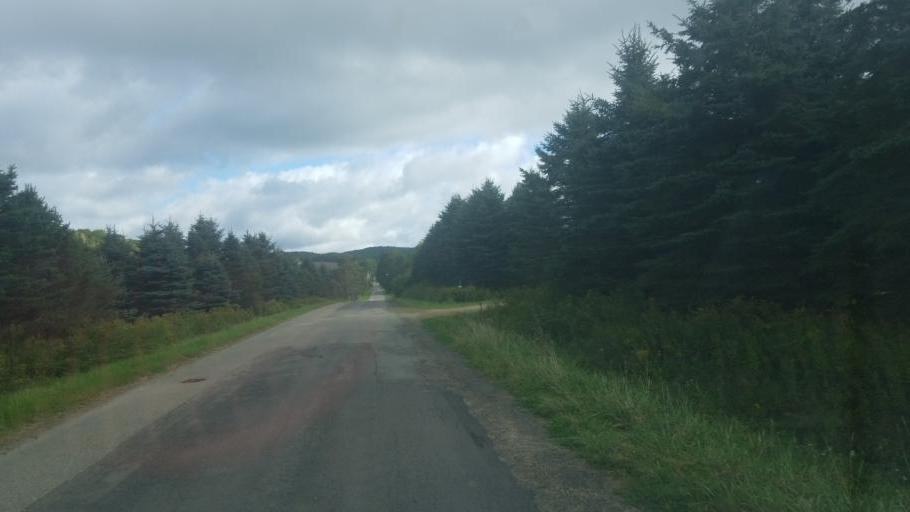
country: US
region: New York
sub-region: Cattaraugus County
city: Weston Mills
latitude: 42.1213
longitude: -78.3080
